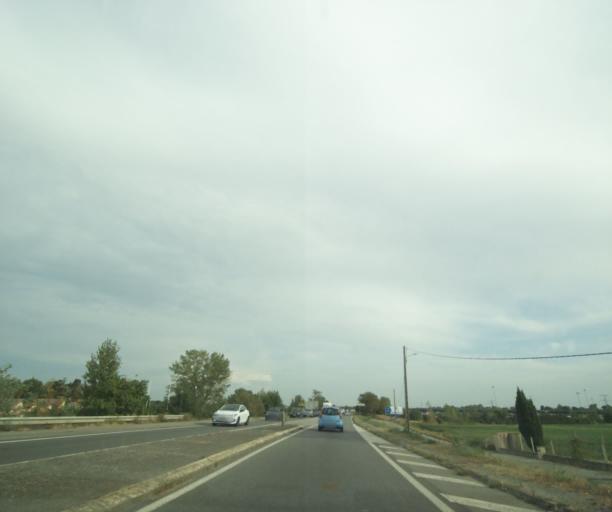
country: FR
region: Midi-Pyrenees
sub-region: Departement de la Haute-Garonne
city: Castelnau-d'Estretefonds
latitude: 43.7877
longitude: 1.3462
